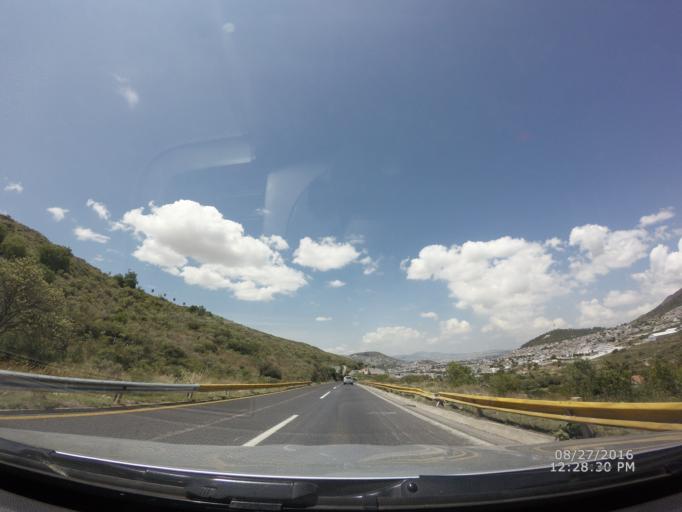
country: MX
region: Hidalgo
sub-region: Mineral de la Reforma
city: Manuel Avila Camacho
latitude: 20.1190
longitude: -98.7054
